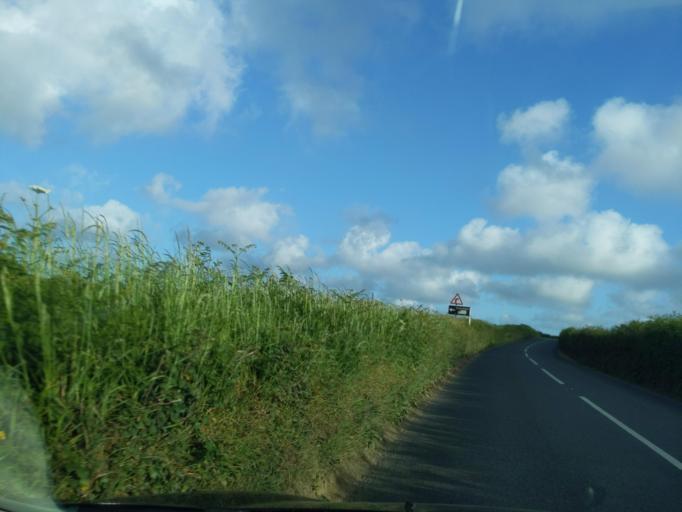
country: GB
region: England
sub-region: Devon
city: Fremington
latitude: 51.0370
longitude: -4.0990
